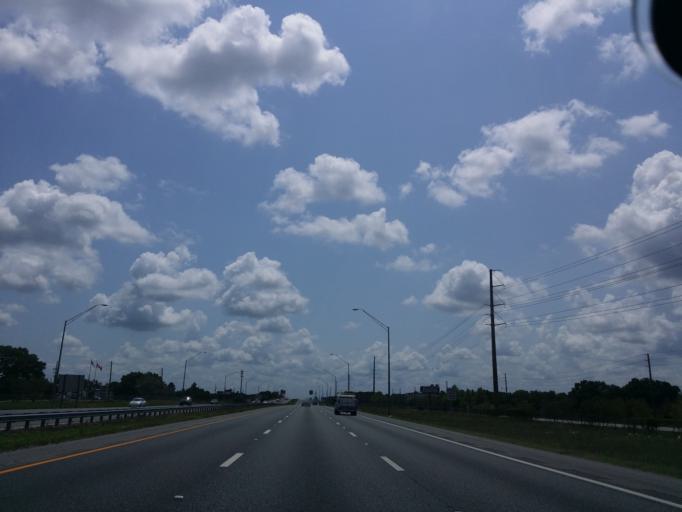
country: US
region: Florida
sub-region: Marion County
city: Ocala
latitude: 29.1756
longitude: -82.1850
